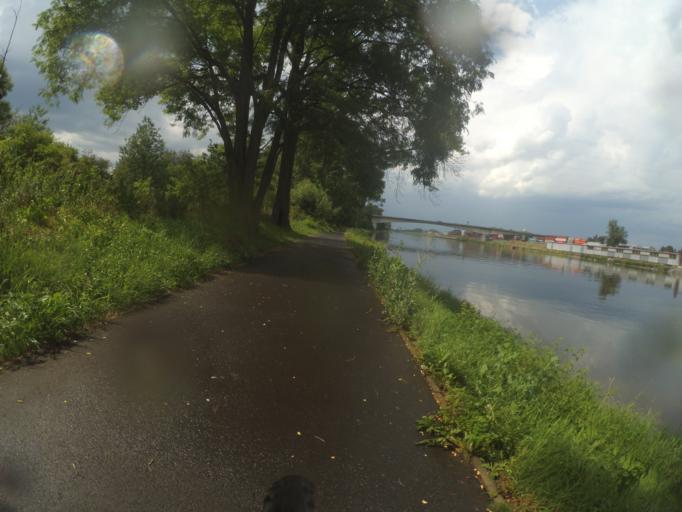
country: CZ
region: Central Bohemia
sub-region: Okres Melnik
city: Melnik
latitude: 50.3553
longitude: 14.4632
